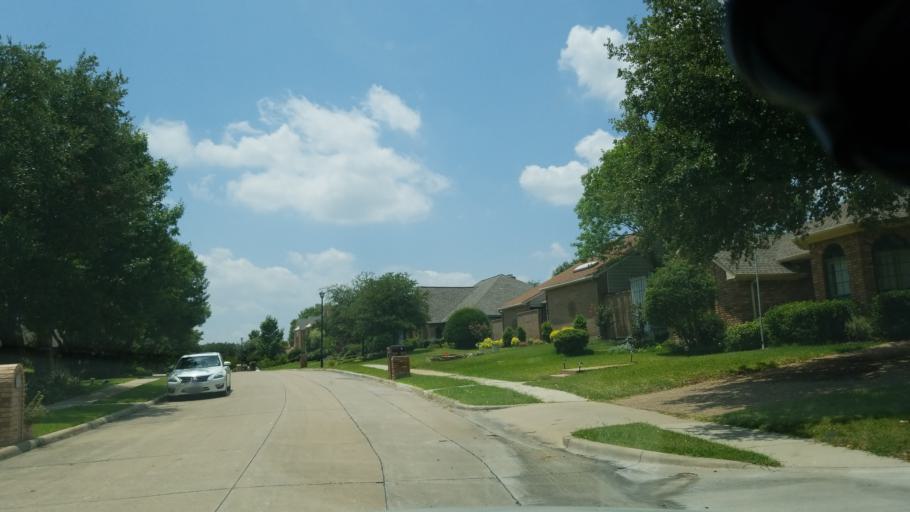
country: US
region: Texas
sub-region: Dallas County
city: Carrollton
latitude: 32.9697
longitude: -96.8782
